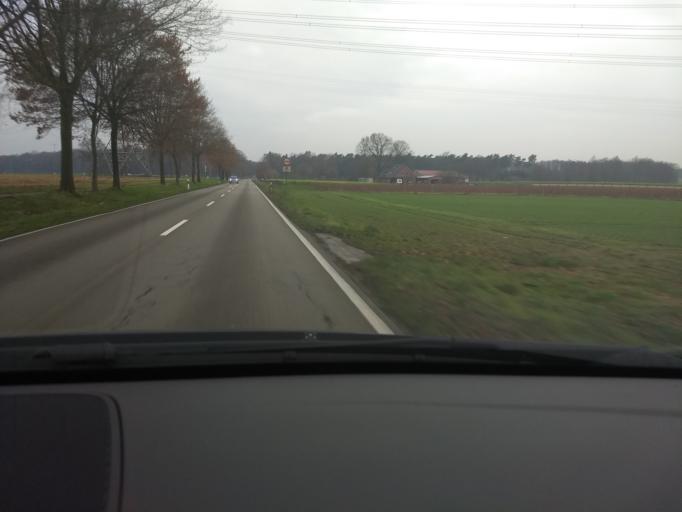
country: DE
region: North Rhine-Westphalia
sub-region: Regierungsbezirk Munster
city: Borken
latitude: 51.8674
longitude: 6.8955
